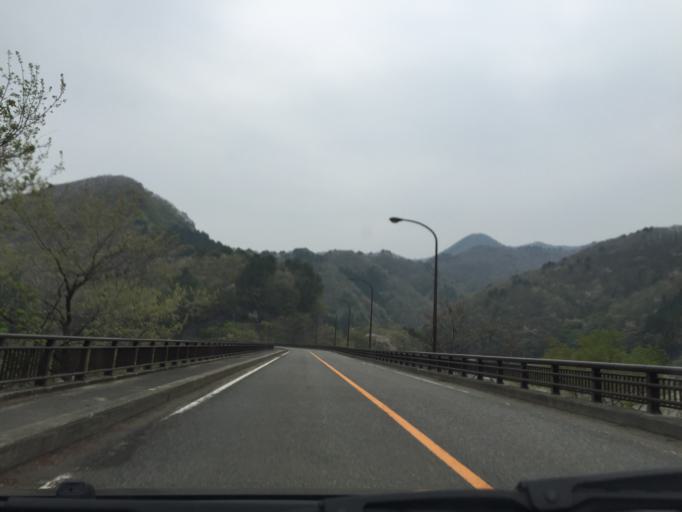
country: JP
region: Tochigi
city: Nikko
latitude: 36.9463
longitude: 139.7005
